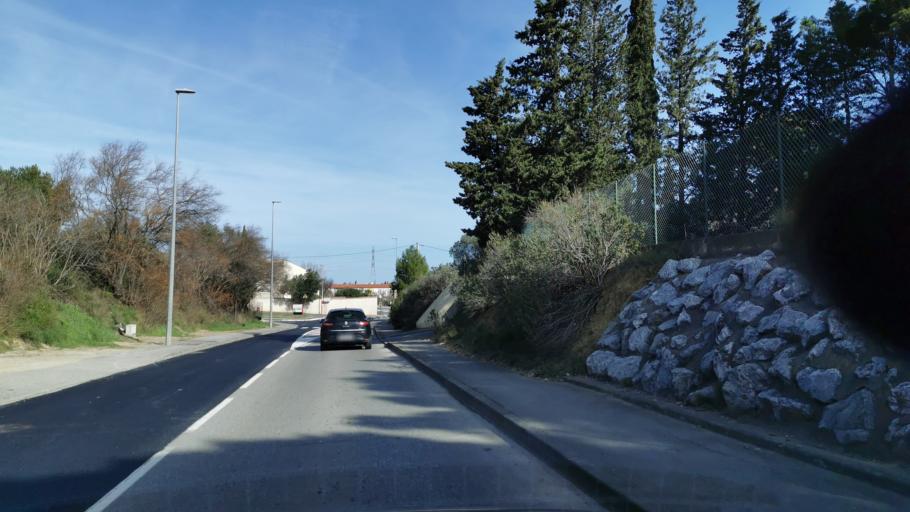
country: FR
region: Languedoc-Roussillon
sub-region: Departement de l'Aude
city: Narbonne
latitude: 43.1655
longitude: 2.9814
